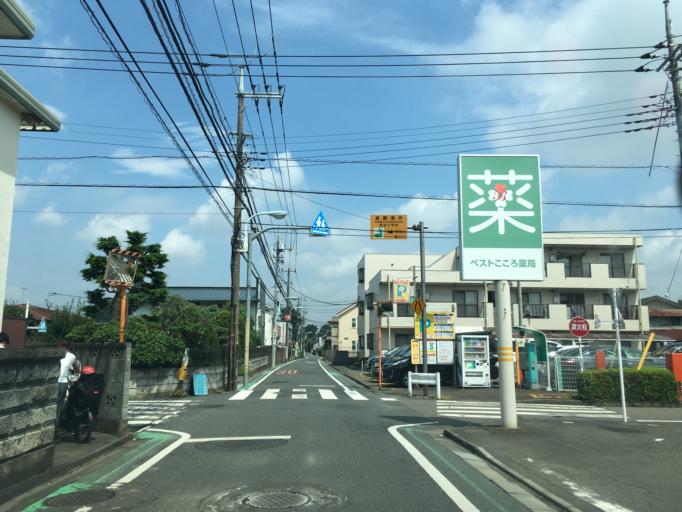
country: JP
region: Tokyo
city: Kokubunji
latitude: 35.6753
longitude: 139.5012
